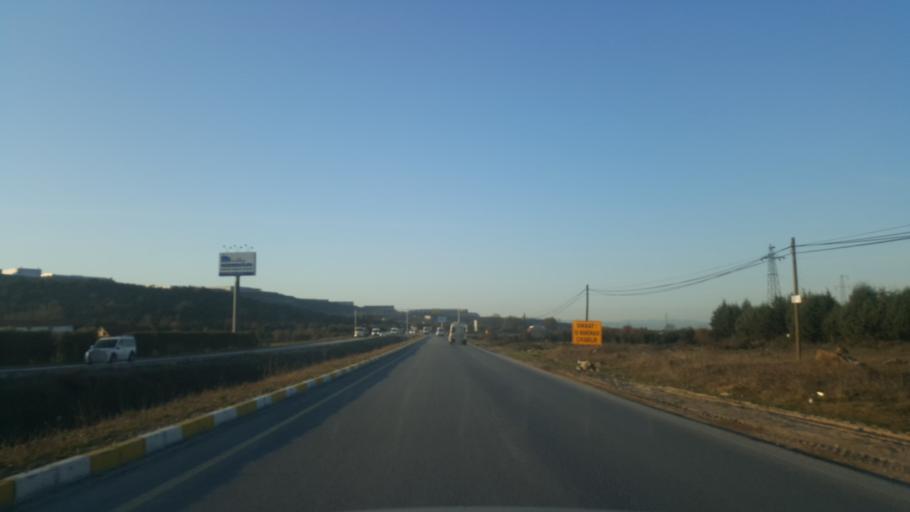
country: TR
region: Kocaeli
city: Tavsanli
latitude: 40.8572
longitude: 29.5566
